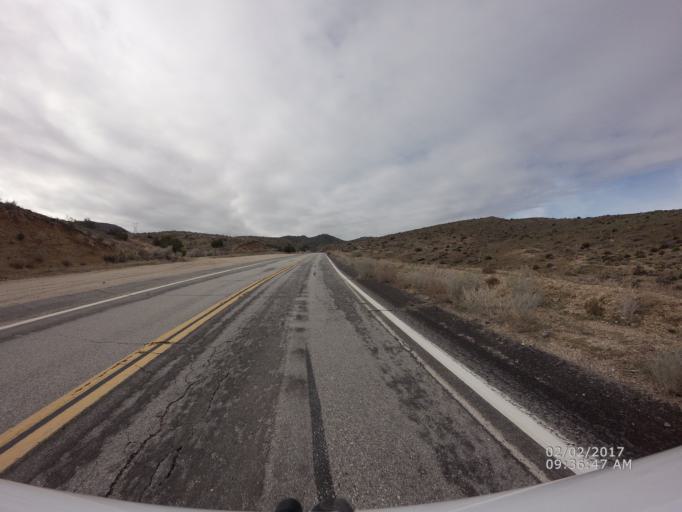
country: US
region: California
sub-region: Los Angeles County
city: Vincent
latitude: 34.4971
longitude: -118.0620
